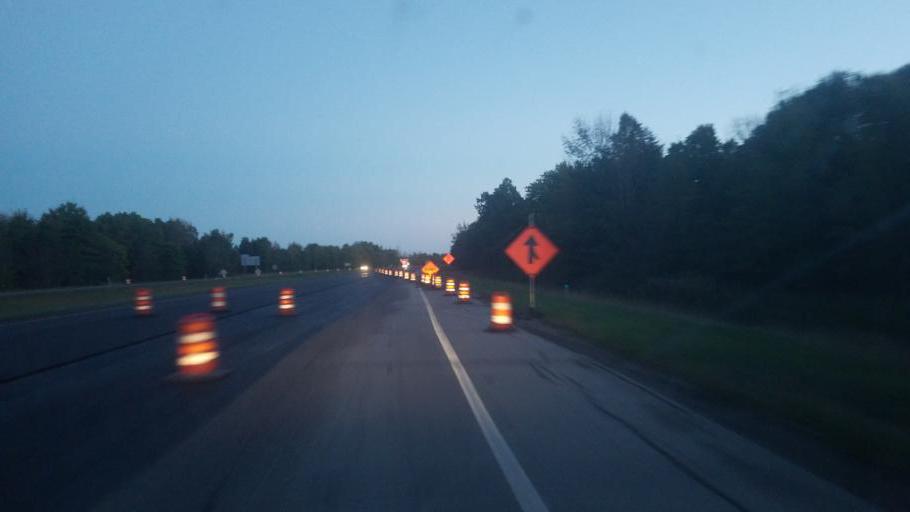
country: US
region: Ohio
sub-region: Ashtabula County
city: Jefferson
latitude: 41.7482
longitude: -80.7103
